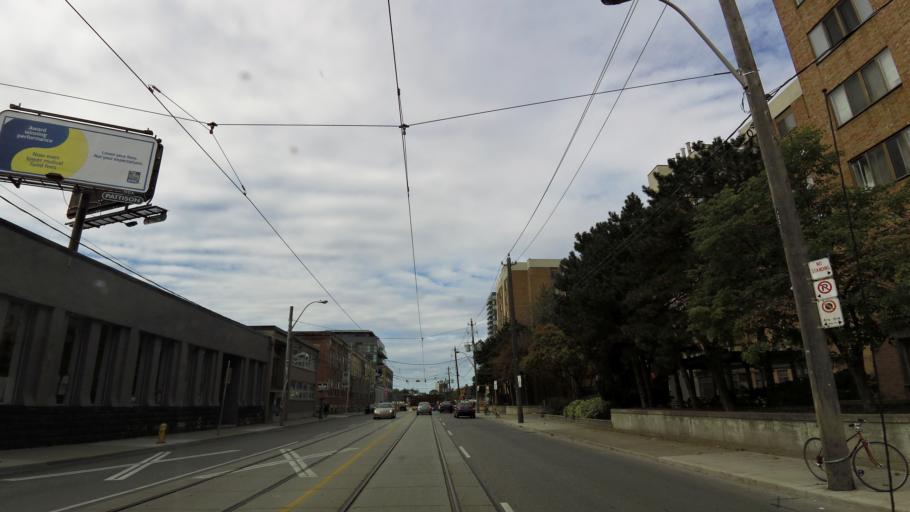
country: CA
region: Ontario
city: Toronto
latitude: 43.6405
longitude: -79.4281
